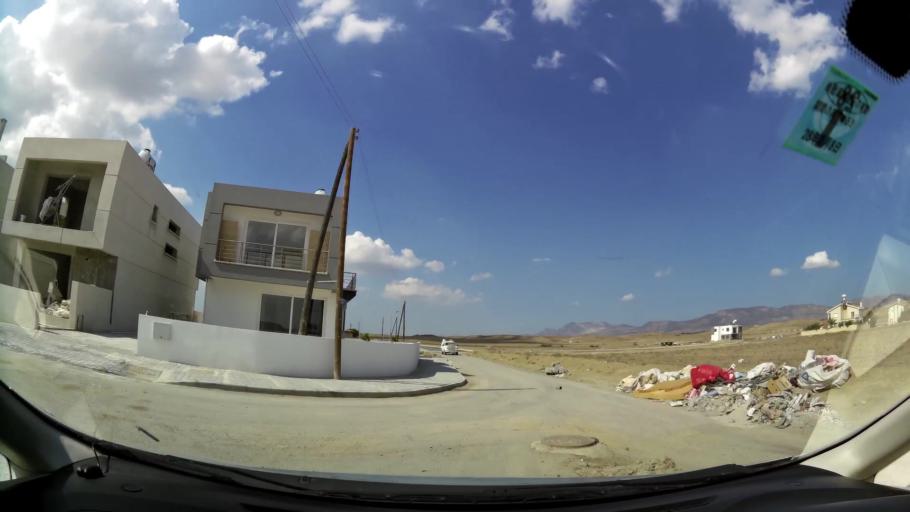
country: CY
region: Lefkosia
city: Nicosia
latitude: 35.2236
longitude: 33.2903
